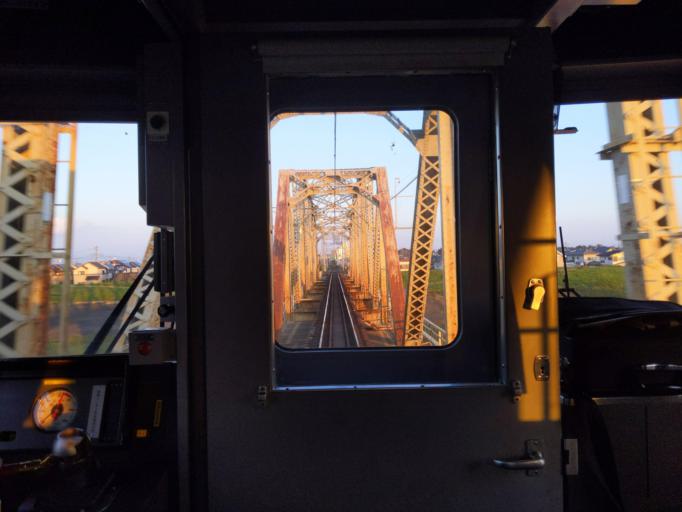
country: JP
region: Chiba
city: Noda
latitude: 35.9796
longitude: 139.8261
